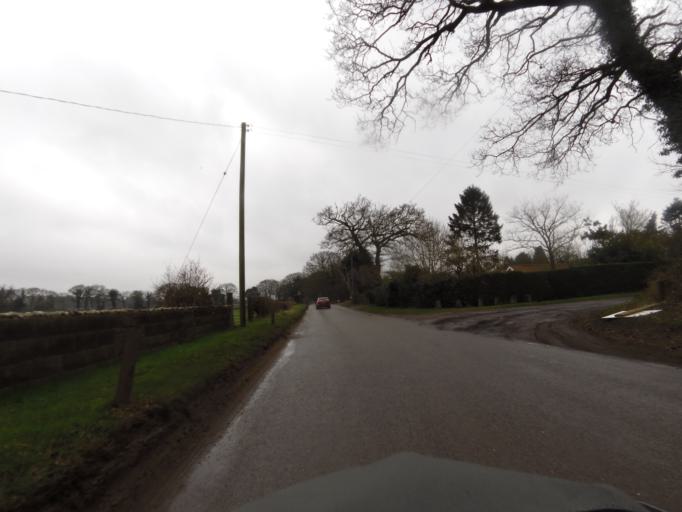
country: GB
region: England
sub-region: Norfolk
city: Briston
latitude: 52.8850
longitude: 1.0814
